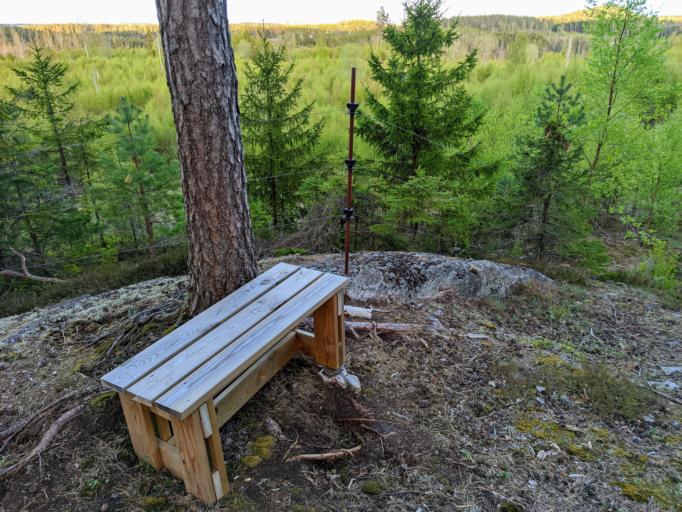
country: NO
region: Ostfold
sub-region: Spydeberg
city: Spydeberg
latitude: 59.6000
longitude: 11.0828
